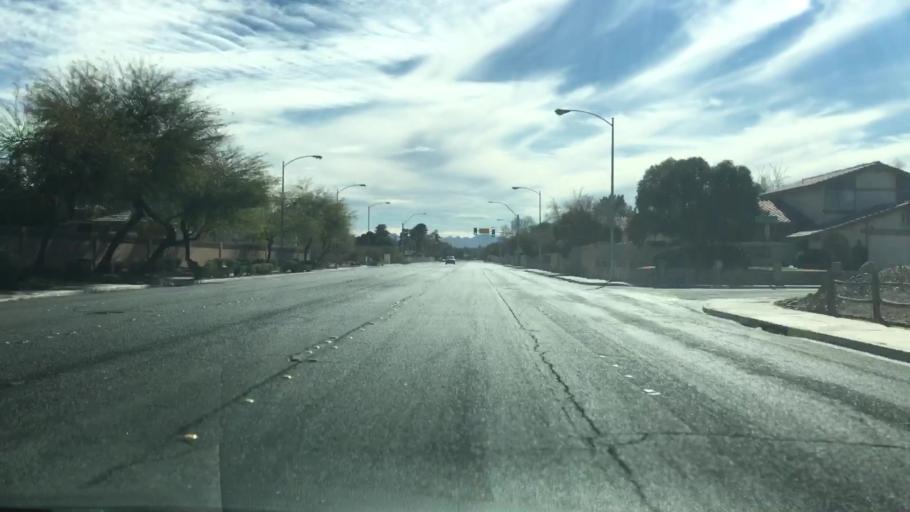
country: US
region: Nevada
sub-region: Clark County
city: Paradise
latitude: 36.0546
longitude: -115.1409
